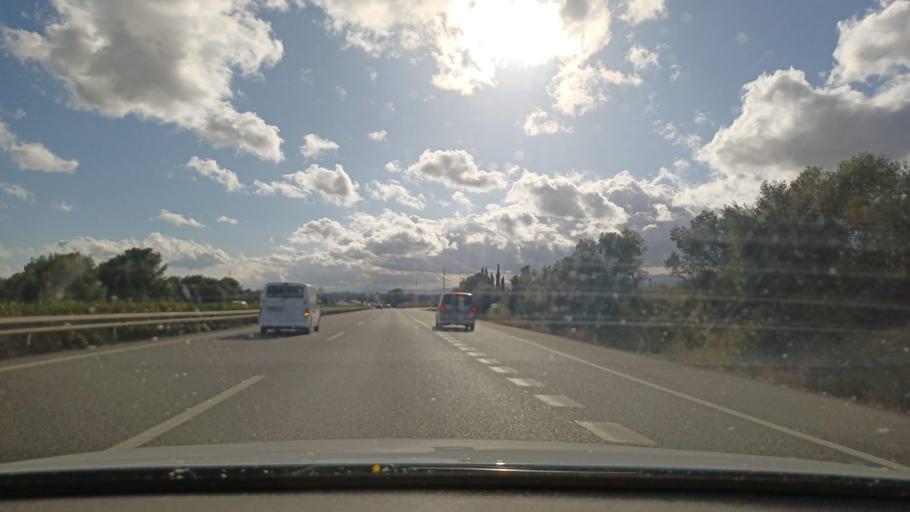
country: ES
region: Catalonia
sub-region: Provincia de Tarragona
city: Camarles
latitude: 40.7580
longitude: 0.6118
